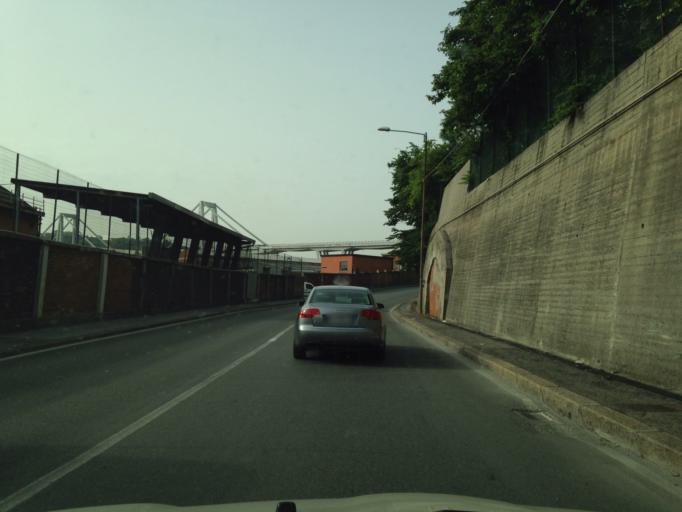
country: IT
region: Liguria
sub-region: Provincia di Genova
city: San Teodoro
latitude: 44.4312
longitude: 8.8868
